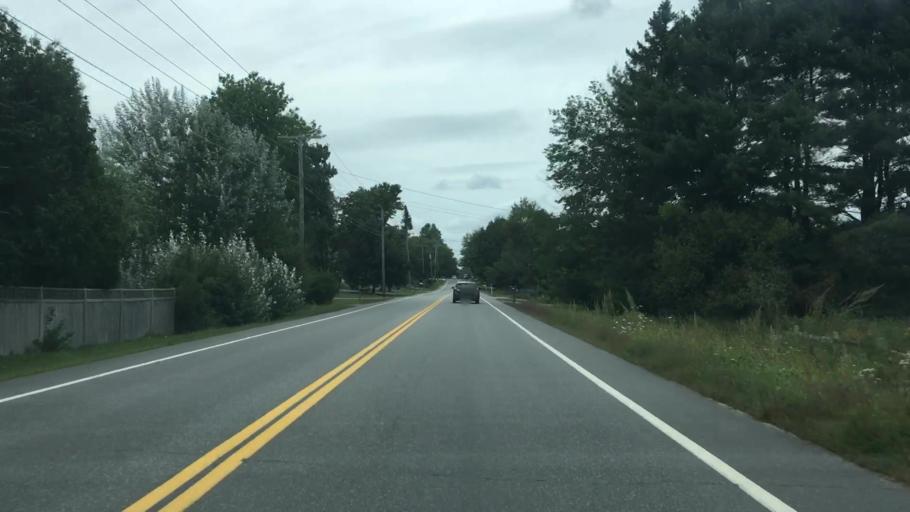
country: US
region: Maine
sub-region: Cumberland County
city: Yarmouth
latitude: 43.8202
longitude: -70.1873
